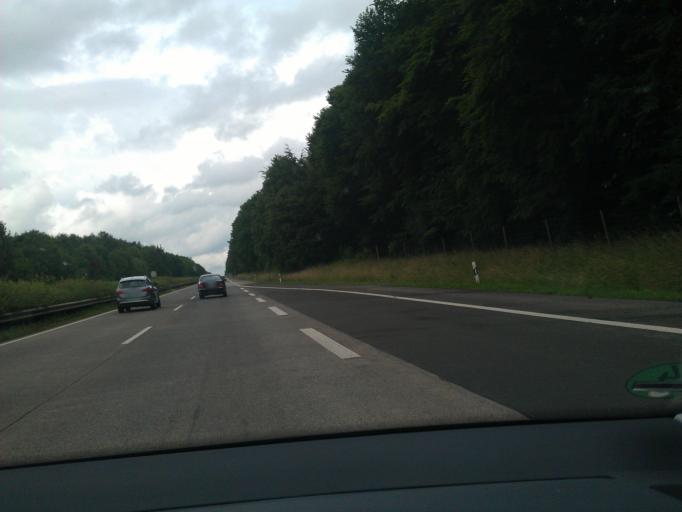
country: DE
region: Rheinland-Pfalz
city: Fohren
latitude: 49.8373
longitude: 6.7698
